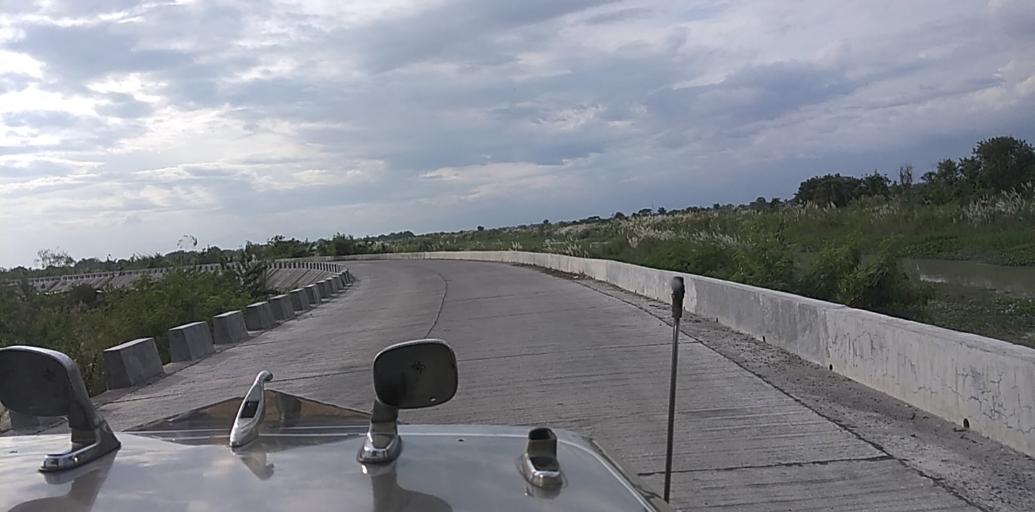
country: PH
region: Central Luzon
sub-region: Province of Pampanga
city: Minalin
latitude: 14.9675
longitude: 120.6659
